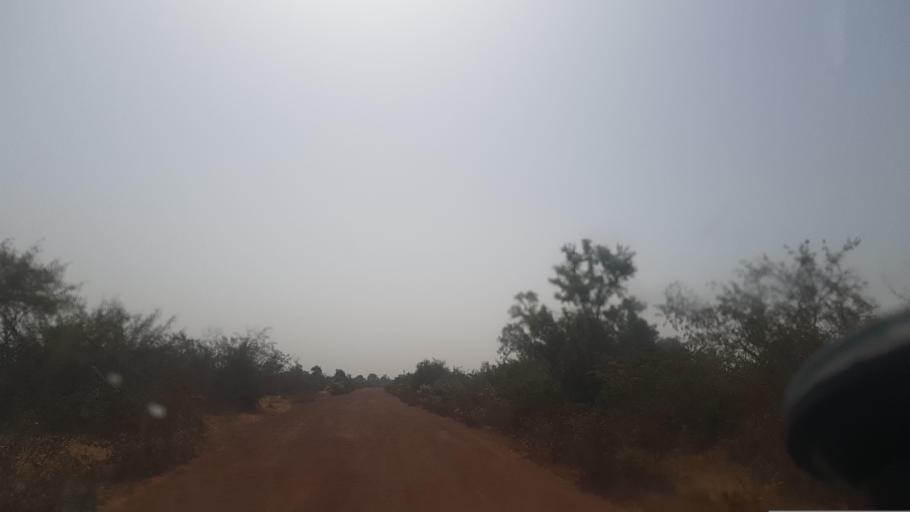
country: ML
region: Segou
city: Baroueli
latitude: 13.0636
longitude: -6.4748
